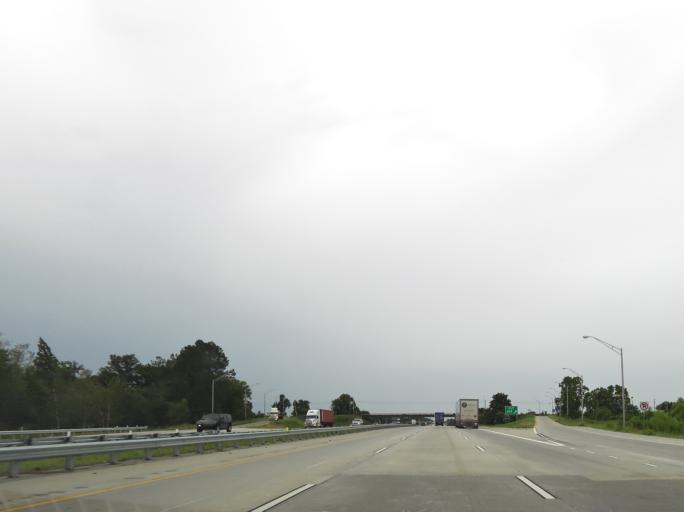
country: US
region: Georgia
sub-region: Dooly County
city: Vienna
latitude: 32.0895
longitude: -83.7633
